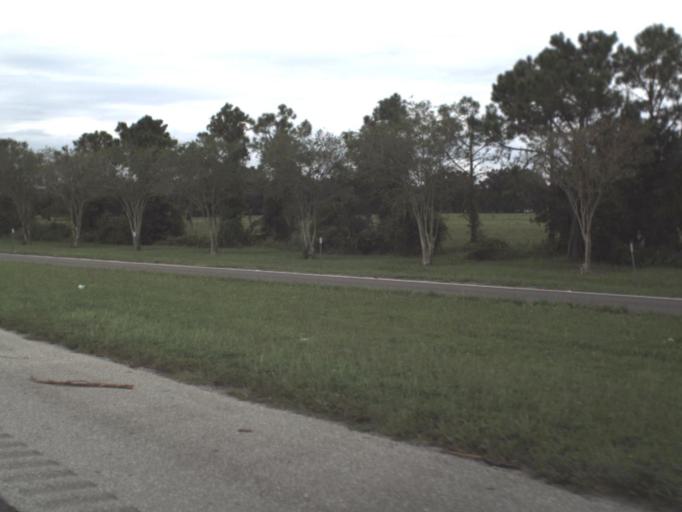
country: US
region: Florida
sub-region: Sarasota County
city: Lake Sarasota
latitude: 27.2661
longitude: -82.4493
